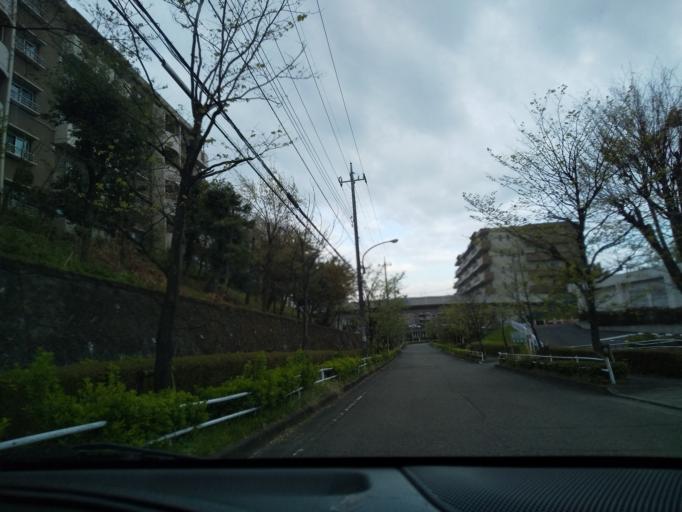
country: JP
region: Tokyo
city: Hino
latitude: 35.6070
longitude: 139.3787
